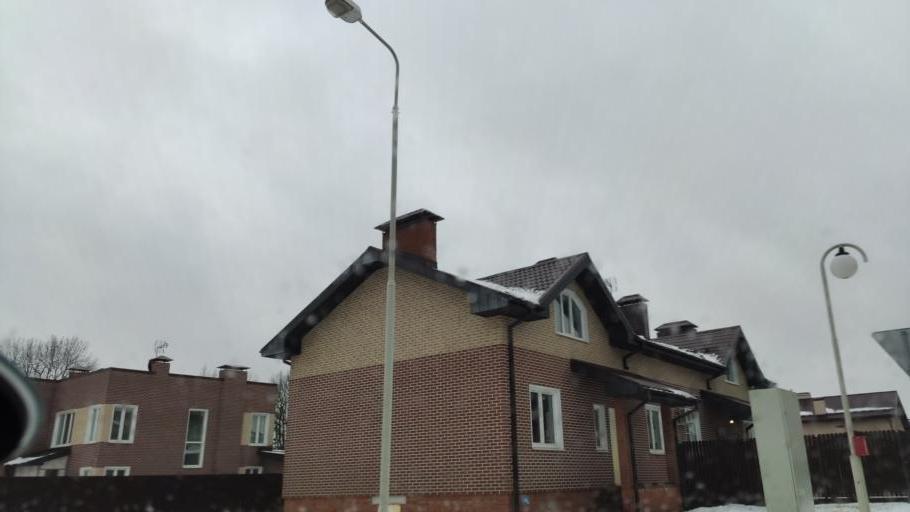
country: RU
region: Moskovskaya
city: Vatutinki
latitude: 55.4293
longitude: 37.3833
